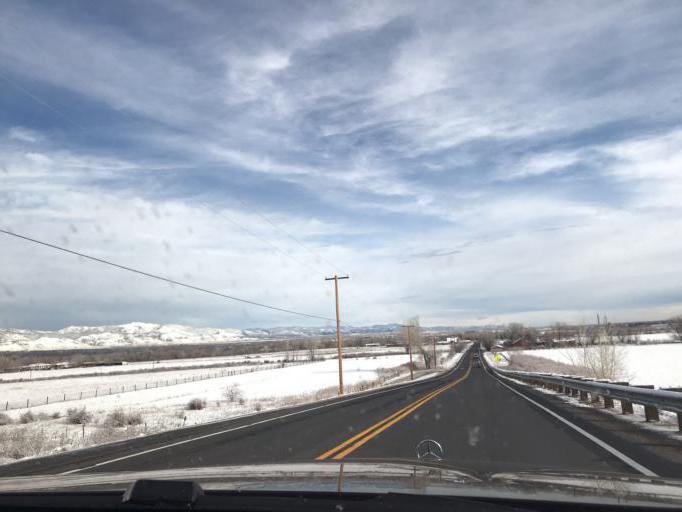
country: US
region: Colorado
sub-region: Boulder County
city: Superior
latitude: 39.9772
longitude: -105.2128
